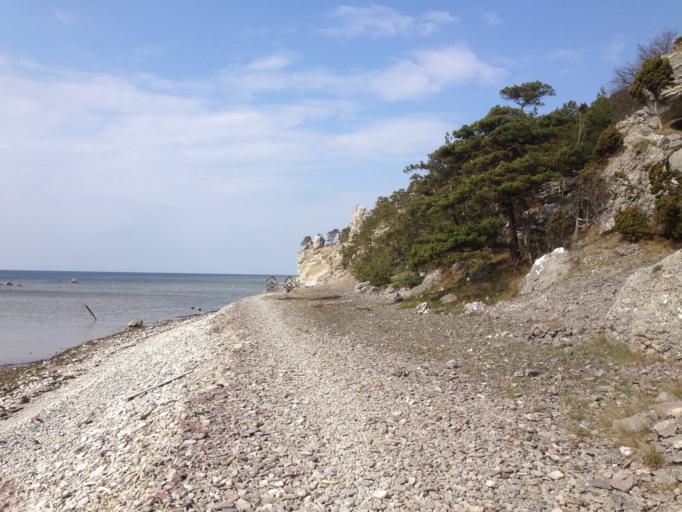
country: SE
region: Gotland
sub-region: Gotland
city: Slite
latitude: 57.8580
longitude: 18.6168
